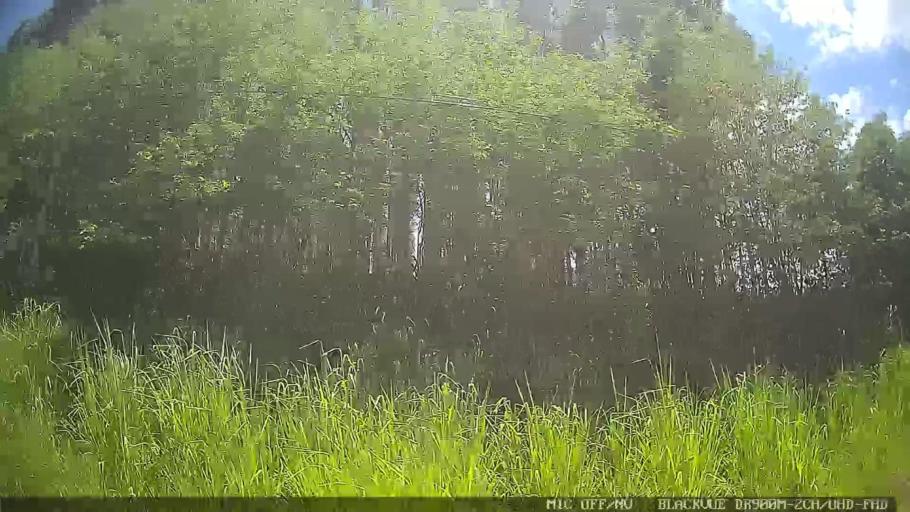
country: BR
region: Sao Paulo
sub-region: Laranjal Paulista
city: Laranjal Paulista
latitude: -23.0249
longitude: -47.8462
